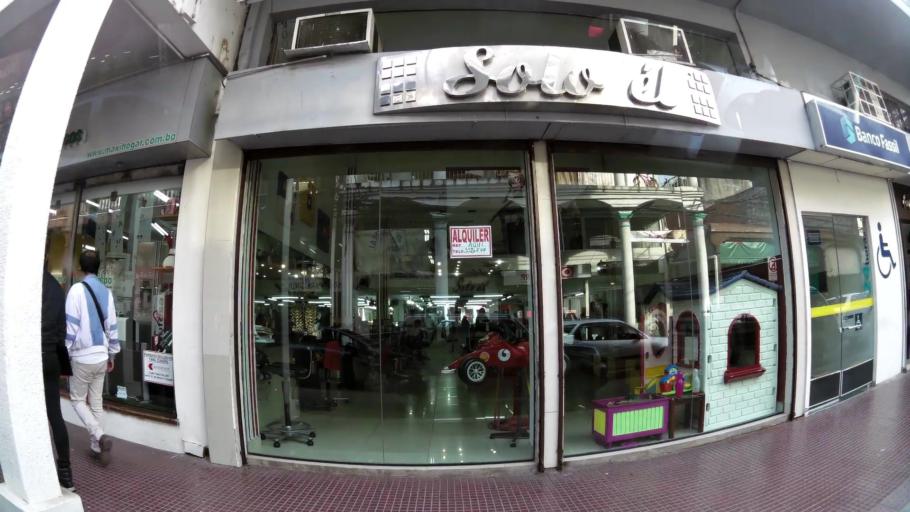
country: BO
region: Santa Cruz
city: Santa Cruz de la Sierra
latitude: -17.7823
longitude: -63.1838
